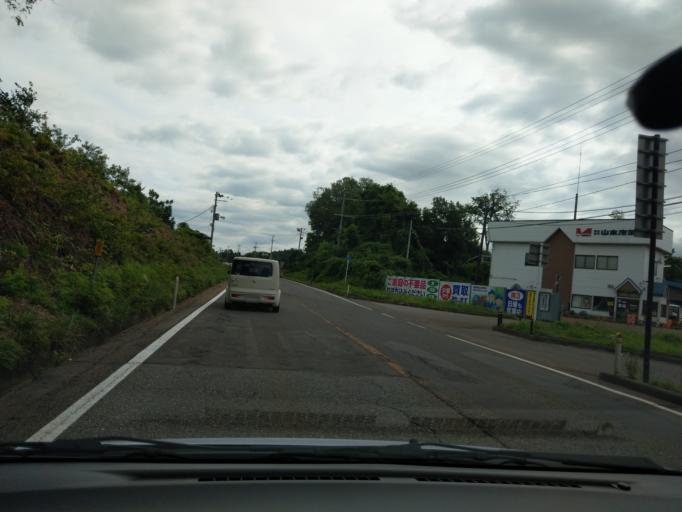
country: JP
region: Akita
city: Yokotemachi
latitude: 39.3441
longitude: 140.5603
